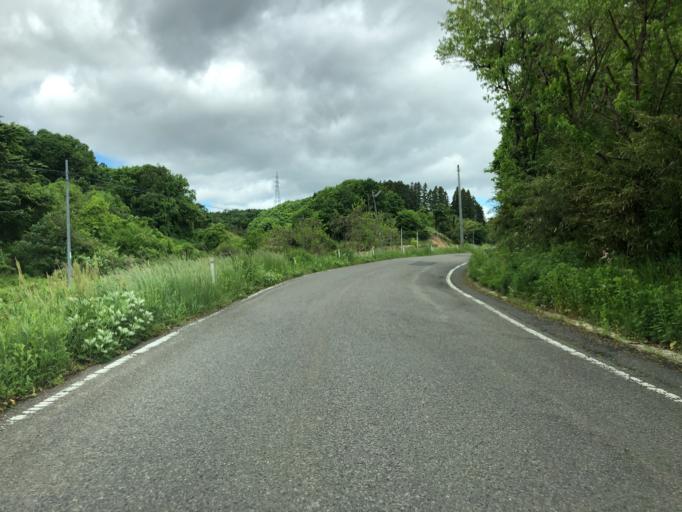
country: JP
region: Fukushima
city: Miharu
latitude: 37.4618
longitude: 140.4693
